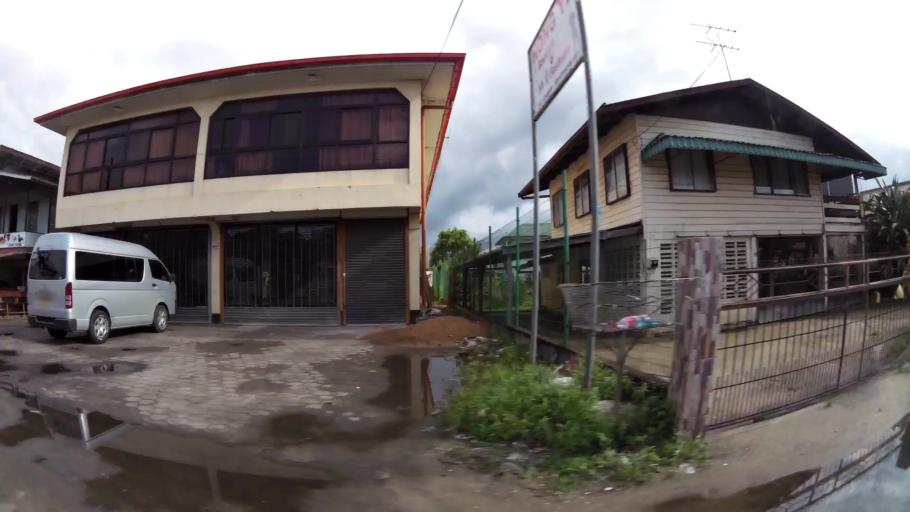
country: SR
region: Paramaribo
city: Paramaribo
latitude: 5.8454
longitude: -55.2254
